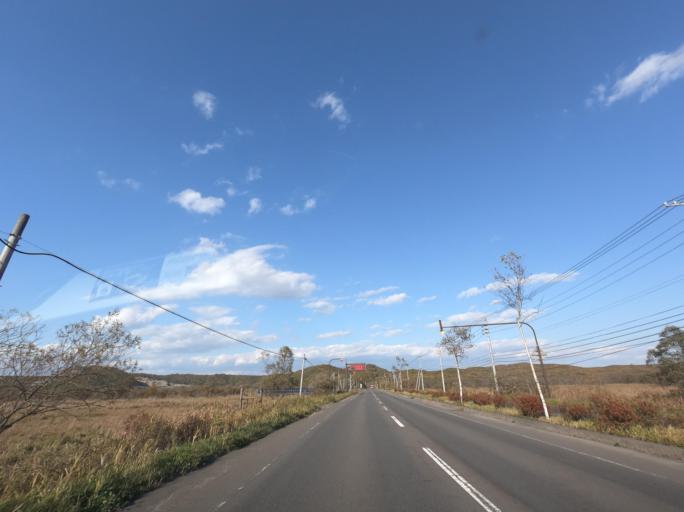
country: JP
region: Hokkaido
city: Kushiro
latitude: 43.0603
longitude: 144.2961
